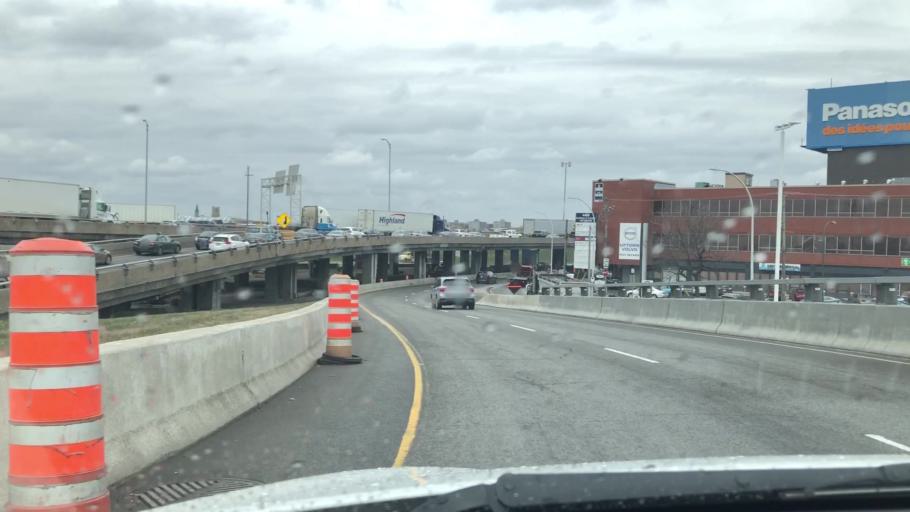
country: CA
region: Quebec
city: Saint-Laurent
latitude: 45.5034
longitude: -73.6642
